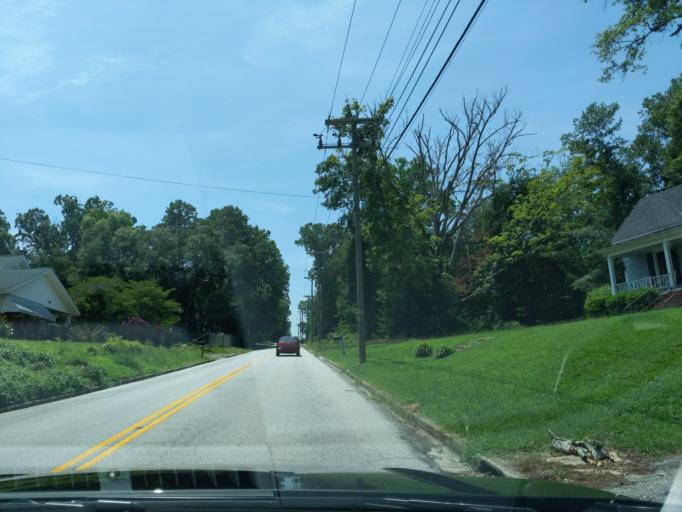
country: US
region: South Carolina
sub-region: Laurens County
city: Laurens
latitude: 34.4916
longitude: -82.0203
